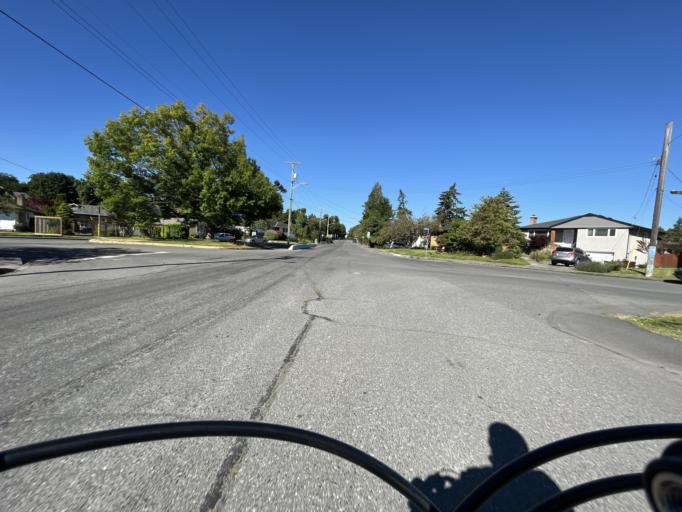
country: CA
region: British Columbia
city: Oak Bay
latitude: 48.4202
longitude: -123.3251
